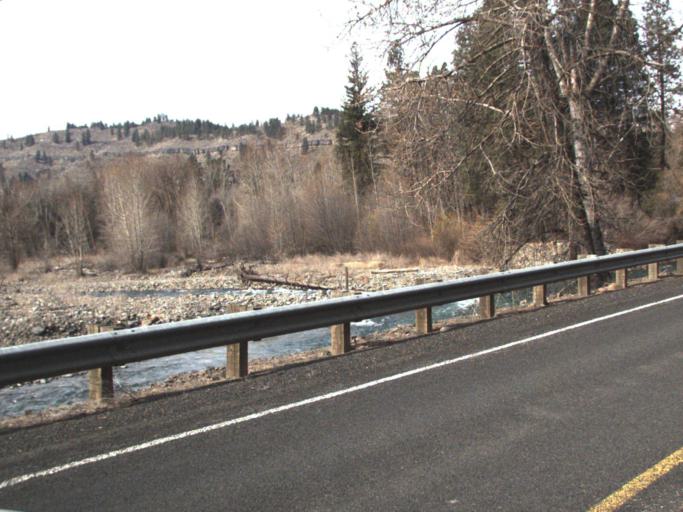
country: US
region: Washington
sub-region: Yakima County
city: Tieton
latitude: 46.8204
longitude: -120.9292
